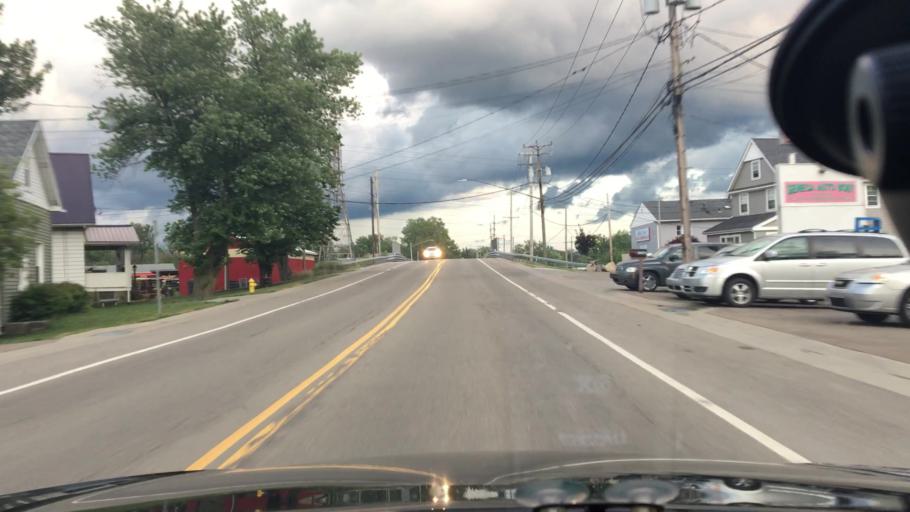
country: US
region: New York
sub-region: Erie County
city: West Seneca
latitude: 42.8387
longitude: -78.7806
